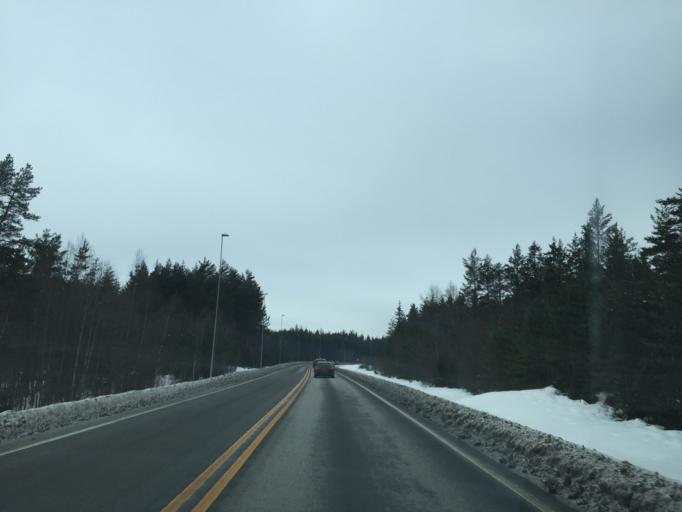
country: NO
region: Hedmark
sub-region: Loten
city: Loten
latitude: 60.7736
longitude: 11.3077
